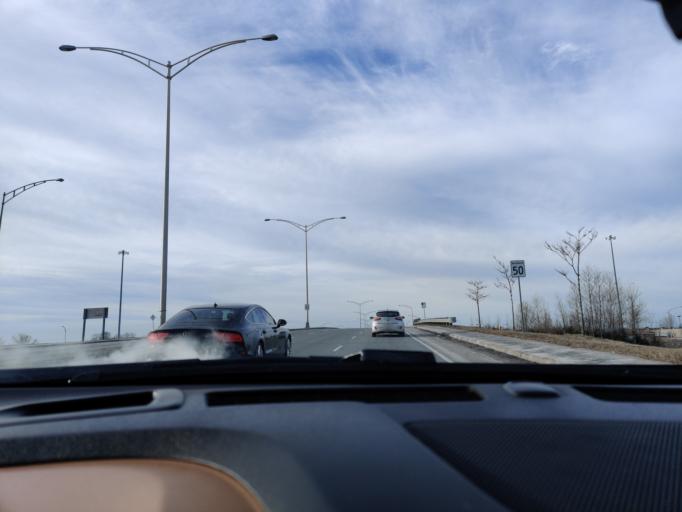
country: CA
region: Quebec
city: Dollard-Des Ormeaux
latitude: 45.5249
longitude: -73.7758
